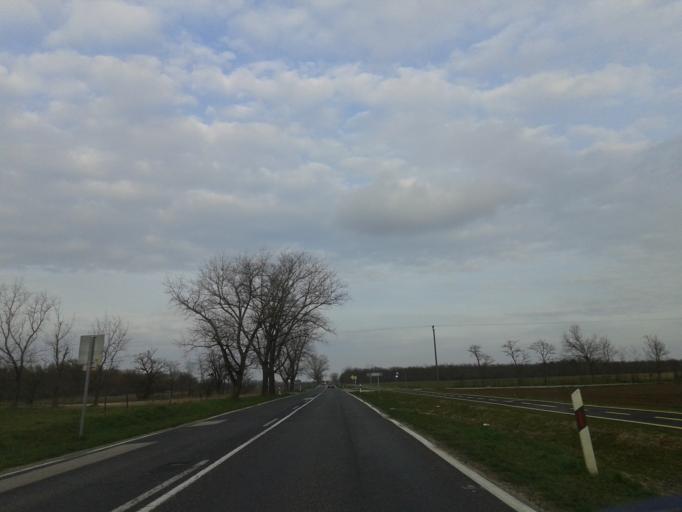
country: HU
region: Gyor-Moson-Sopron
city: Toltestava
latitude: 47.7281
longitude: 17.7354
